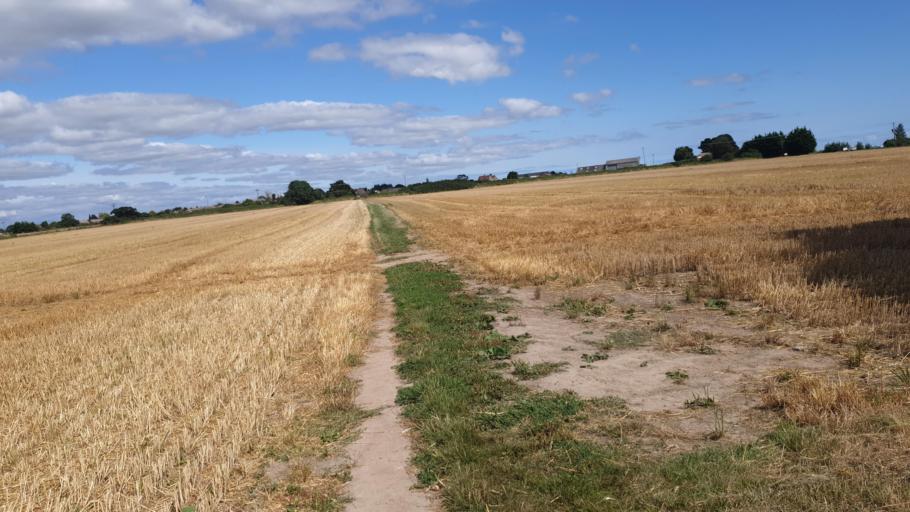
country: GB
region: England
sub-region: Essex
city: Dovercourt
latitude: 51.9120
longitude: 1.2176
